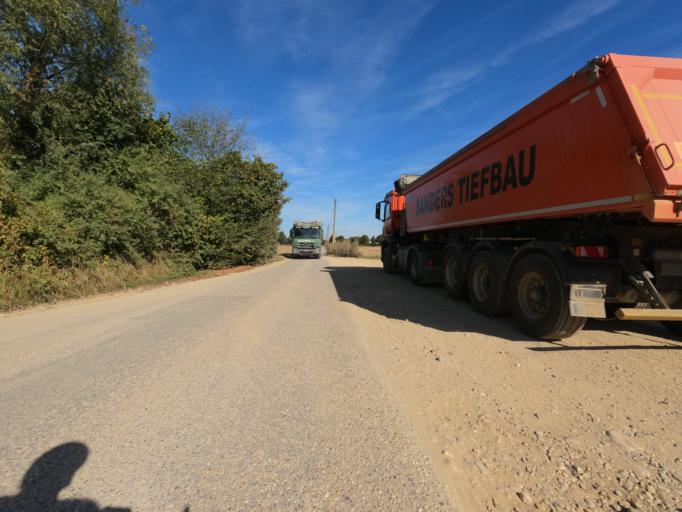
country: DE
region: North Rhine-Westphalia
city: Erkelenz
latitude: 51.0553
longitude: 6.3602
